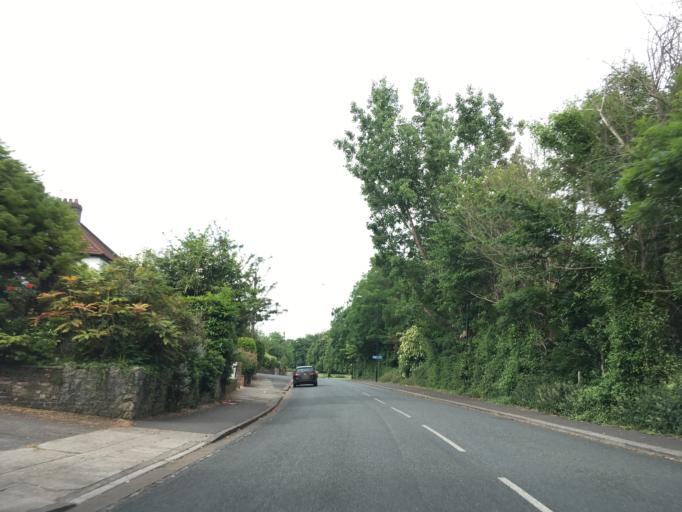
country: GB
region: England
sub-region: Bristol
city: Bristol
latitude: 51.4846
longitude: -2.6434
